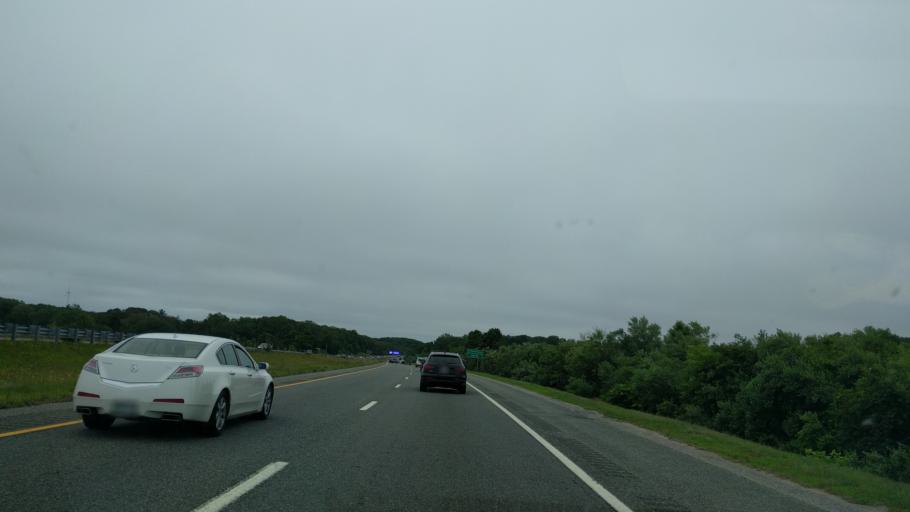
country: US
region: Rhode Island
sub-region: Washington County
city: Exeter
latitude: 41.6013
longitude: -71.4987
